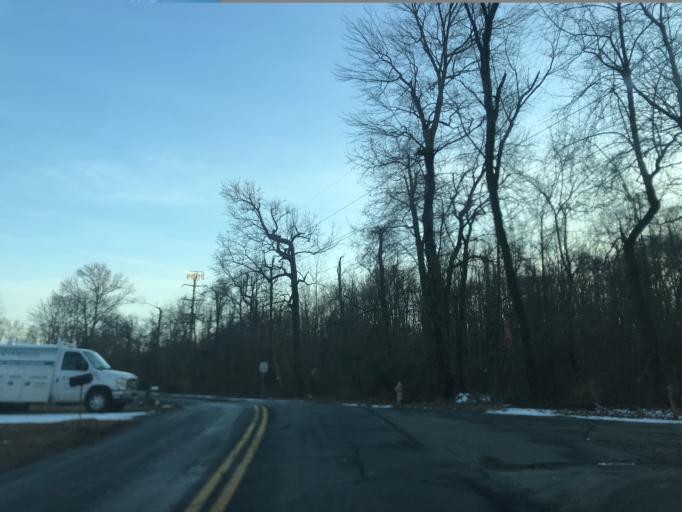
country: US
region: Maryland
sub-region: Harford County
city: Riverside
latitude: 39.4398
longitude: -76.2575
